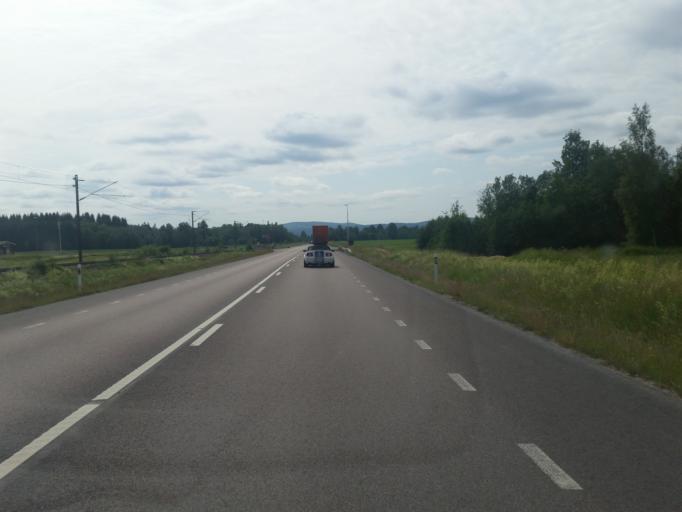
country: SE
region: Dalarna
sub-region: Gagnefs Kommun
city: Djuras
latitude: 60.5763
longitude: 15.1226
